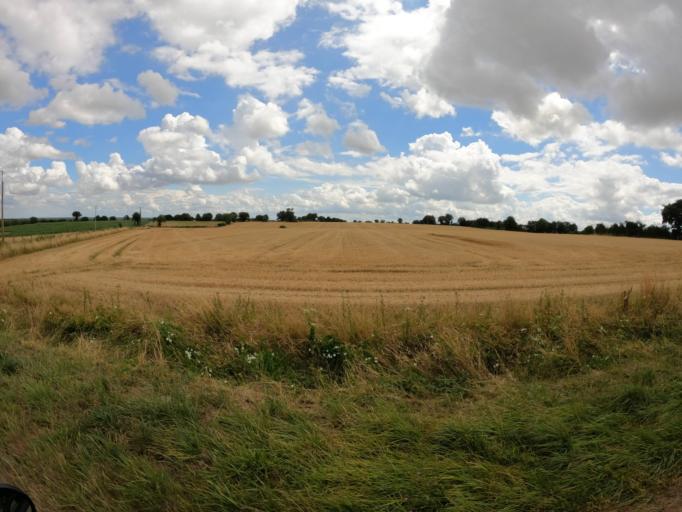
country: FR
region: Pays de la Loire
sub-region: Departement de Maine-et-Loire
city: Morannes
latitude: 47.8016
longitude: -0.4290
